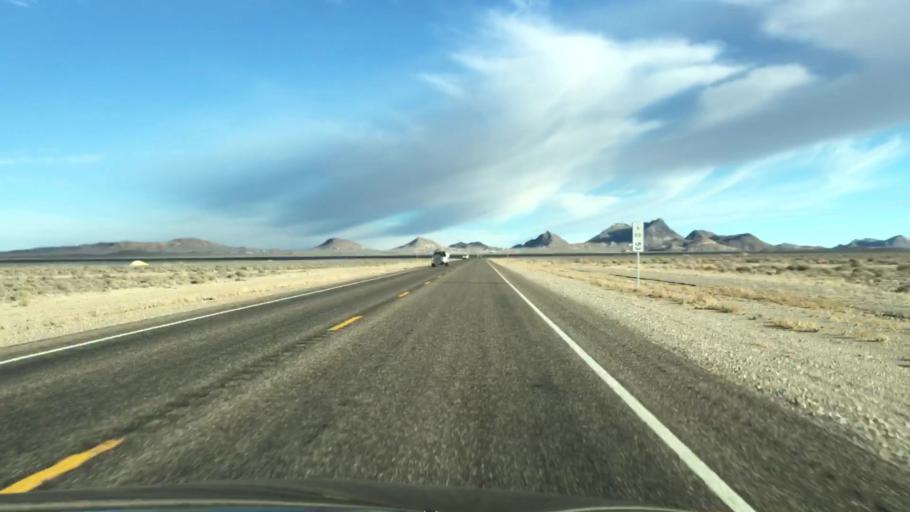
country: US
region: Nevada
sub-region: Nye County
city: Tonopah
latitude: 38.1010
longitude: -117.3315
